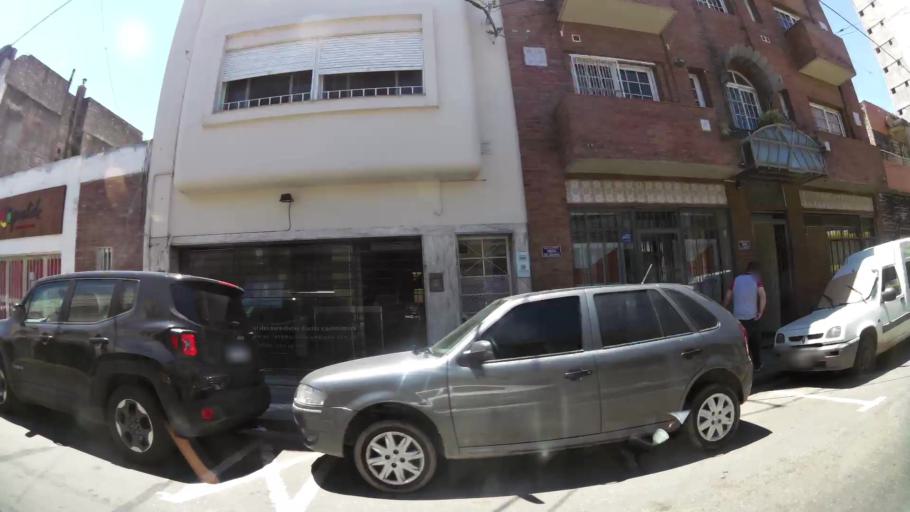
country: AR
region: Santa Fe
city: Santa Fe de la Vera Cruz
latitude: -31.6427
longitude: -60.7090
